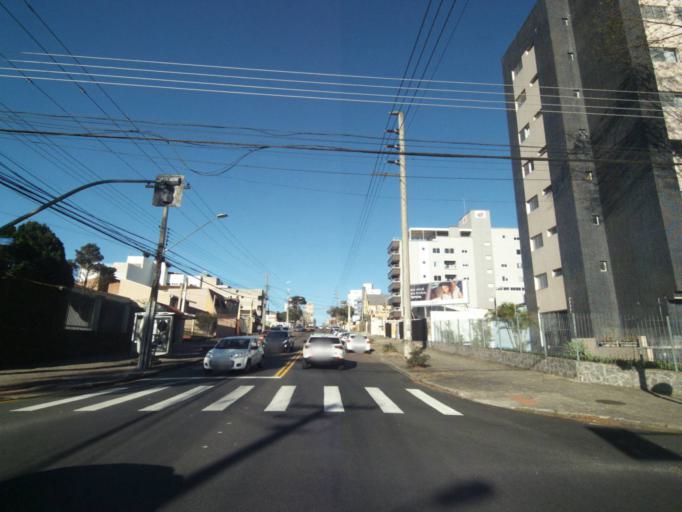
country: BR
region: Parana
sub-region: Curitiba
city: Curitiba
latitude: -25.4607
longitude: -49.2979
